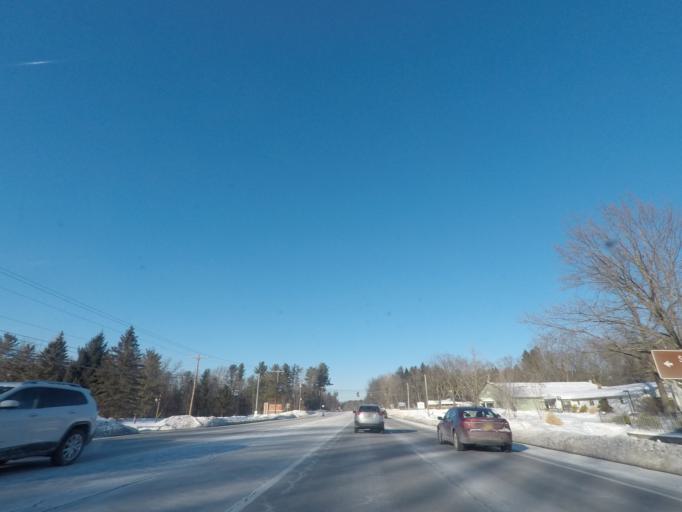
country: US
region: New York
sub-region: Saratoga County
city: Saratoga Springs
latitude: 43.0448
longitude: -73.7902
